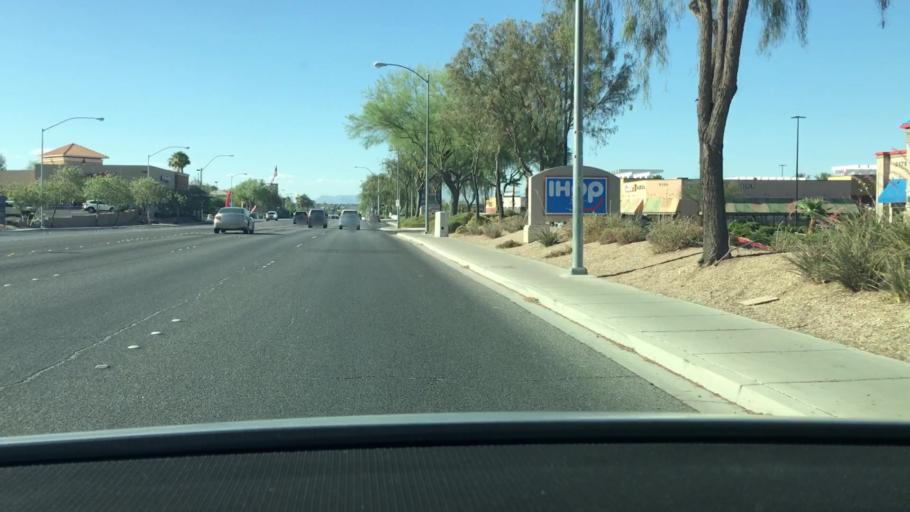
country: US
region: Nevada
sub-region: Clark County
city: Summerlin South
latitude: 36.0948
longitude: -115.2972
